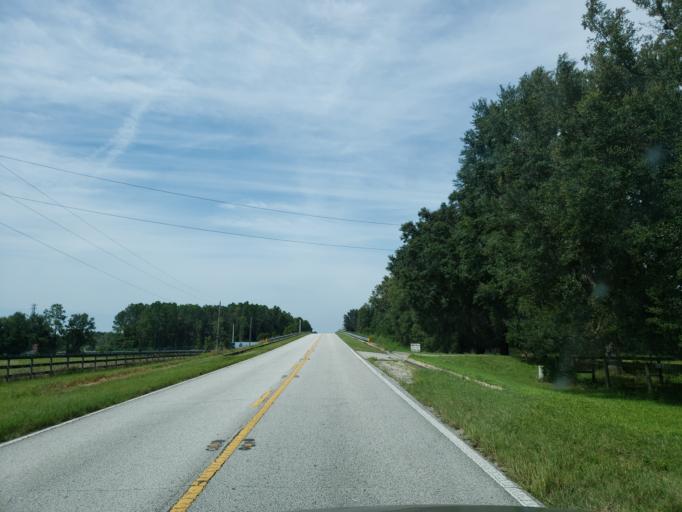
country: US
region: Florida
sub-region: Pasco County
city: San Antonio
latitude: 28.3993
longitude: -82.3118
